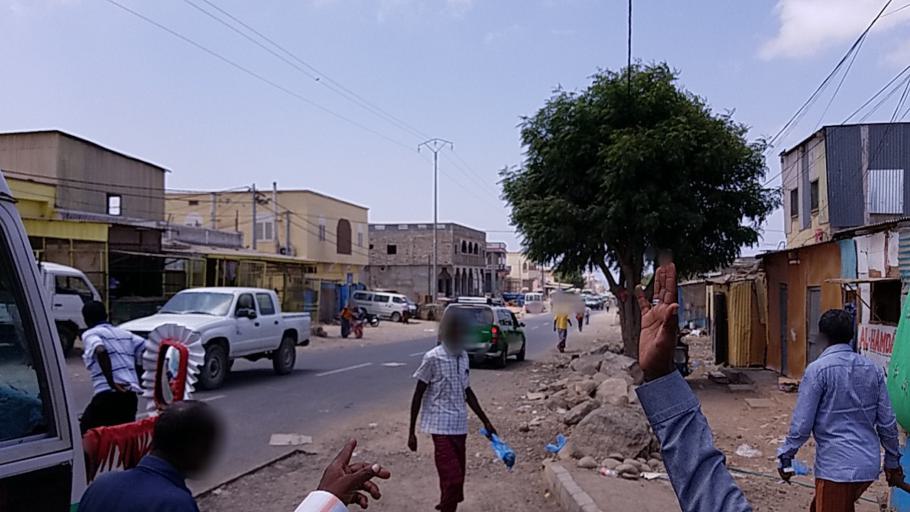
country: DJ
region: Djibouti
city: Djibouti
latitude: 11.5554
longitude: 43.1017
